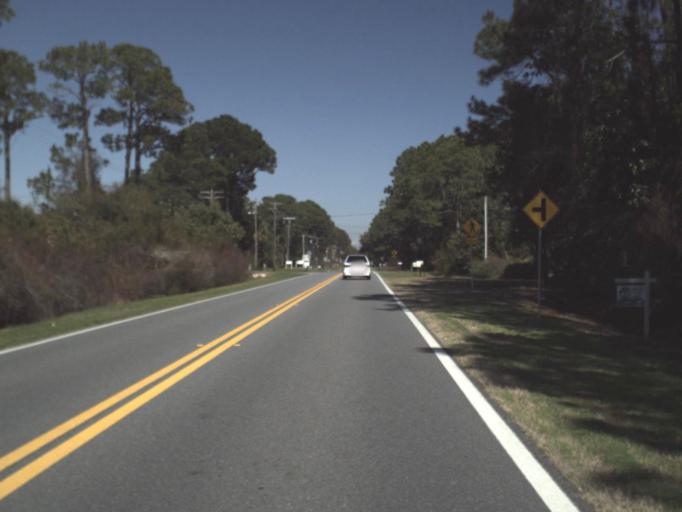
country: US
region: Florida
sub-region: Franklin County
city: Carrabelle
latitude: 29.8816
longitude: -84.5944
